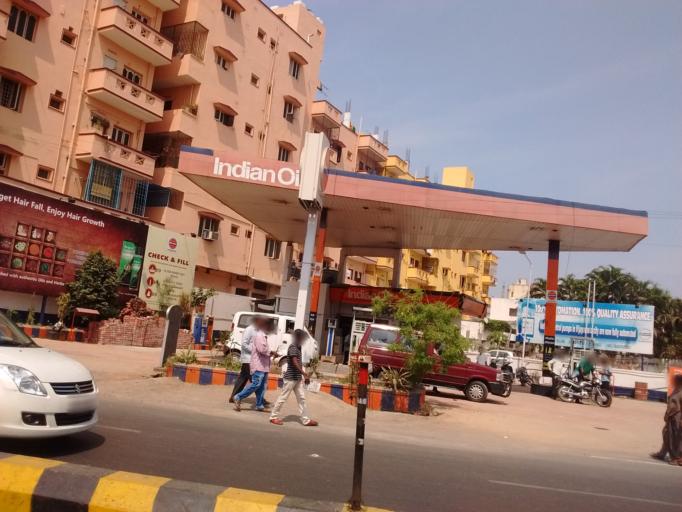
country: IN
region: Andhra Pradesh
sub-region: Krishna
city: Vijayawada
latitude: 16.5158
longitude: 80.6387
